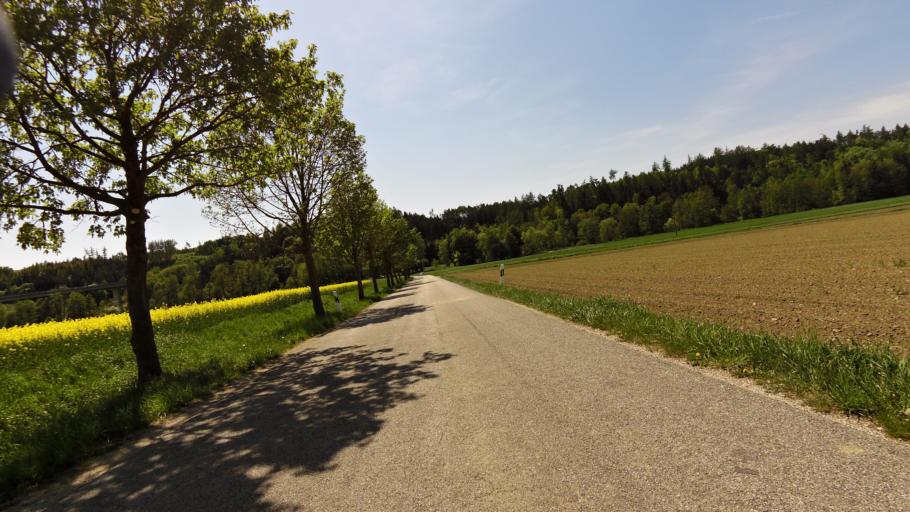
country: DE
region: Bavaria
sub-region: Lower Bavaria
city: Weihmichl
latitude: 48.5680
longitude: 12.0865
